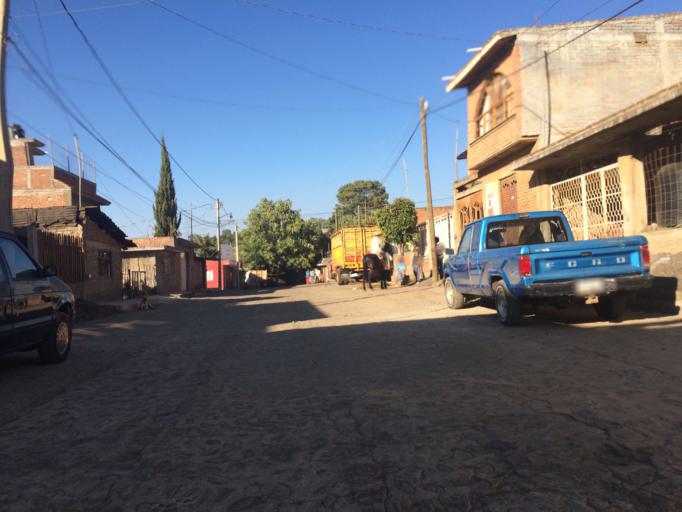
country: MX
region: Michoacan
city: Patzcuaro
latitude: 19.5055
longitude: -101.5978
